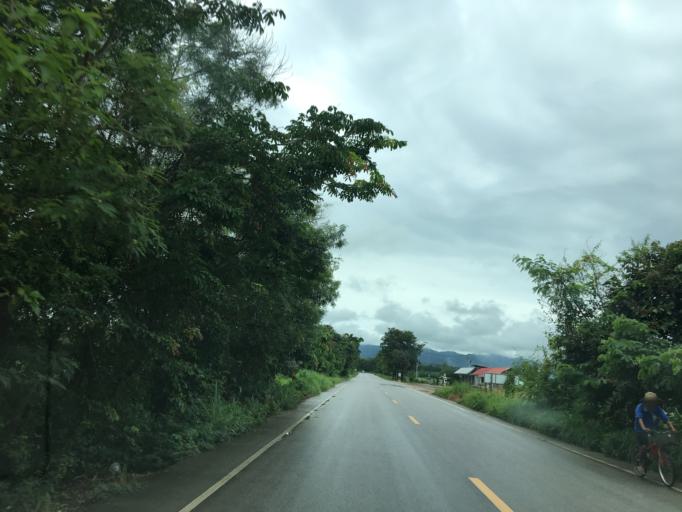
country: TH
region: Chiang Rai
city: Pa Daet
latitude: 19.4982
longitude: 99.9797
